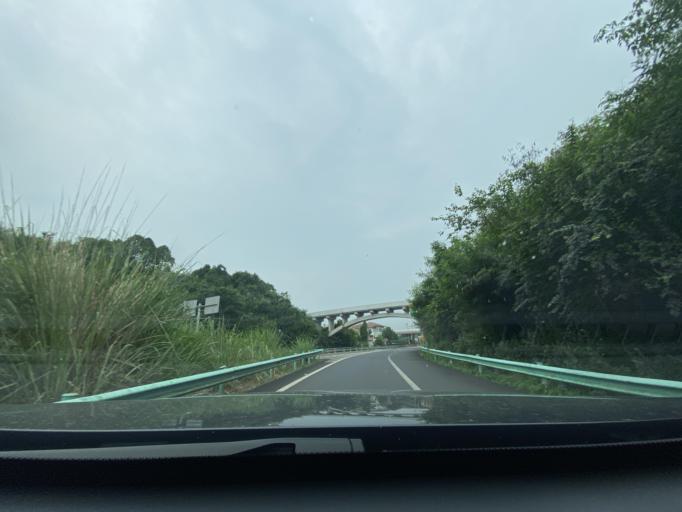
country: CN
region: Sichuan
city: Wenlin
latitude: 30.2948
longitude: 104.1228
